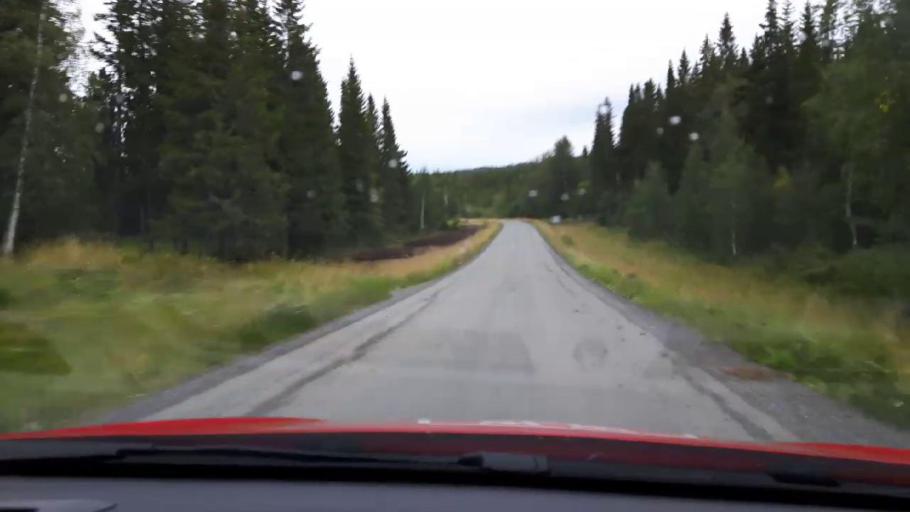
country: SE
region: Jaemtland
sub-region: Are Kommun
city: Jarpen
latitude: 63.4311
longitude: 13.2904
